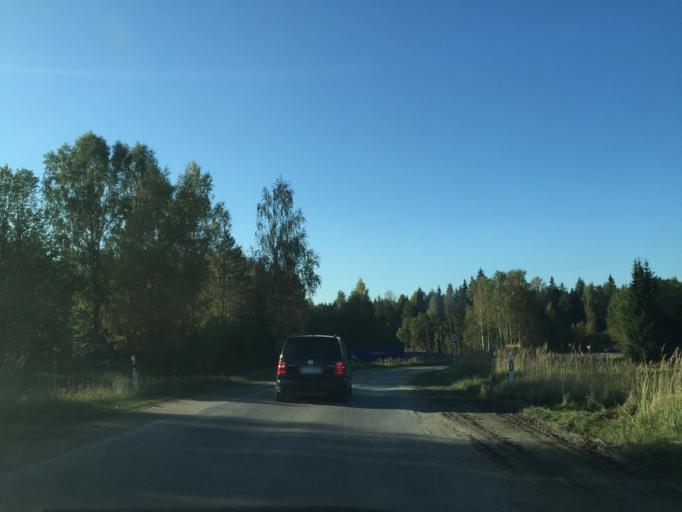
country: LV
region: Amatas Novads
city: Drabesi
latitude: 57.2281
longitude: 25.2545
